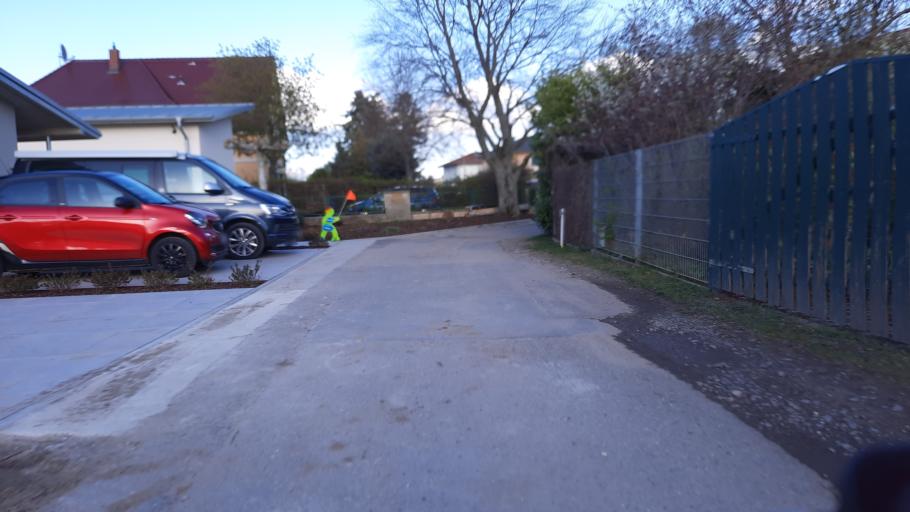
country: DE
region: Rheinland-Pfalz
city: Offstein
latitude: 49.6076
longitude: 8.2641
